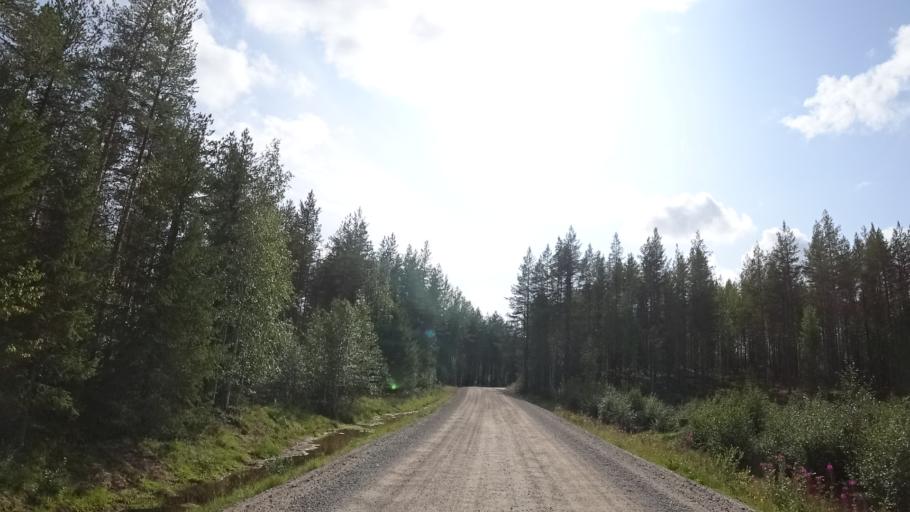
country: FI
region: North Karelia
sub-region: Pielisen Karjala
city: Lieksa
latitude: 63.5724
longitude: 30.1143
